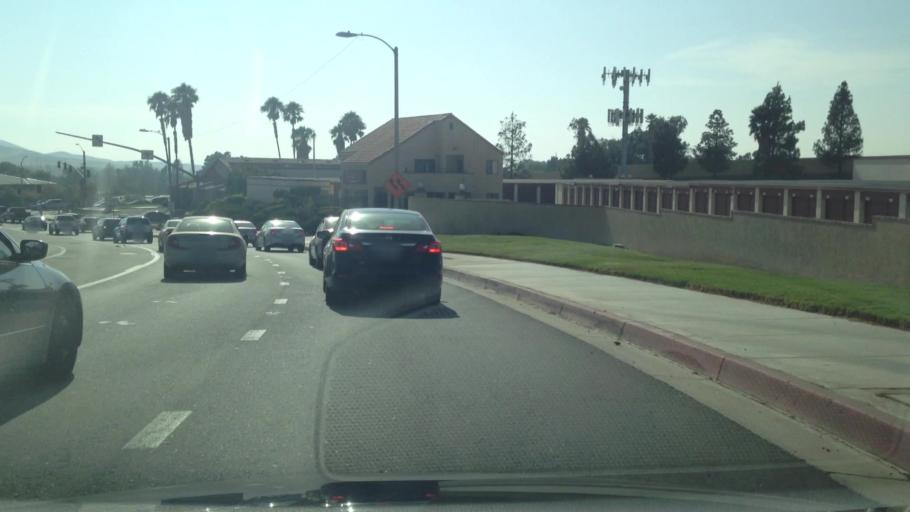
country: US
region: California
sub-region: Riverside County
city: Pedley
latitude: 33.9680
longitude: -117.4648
